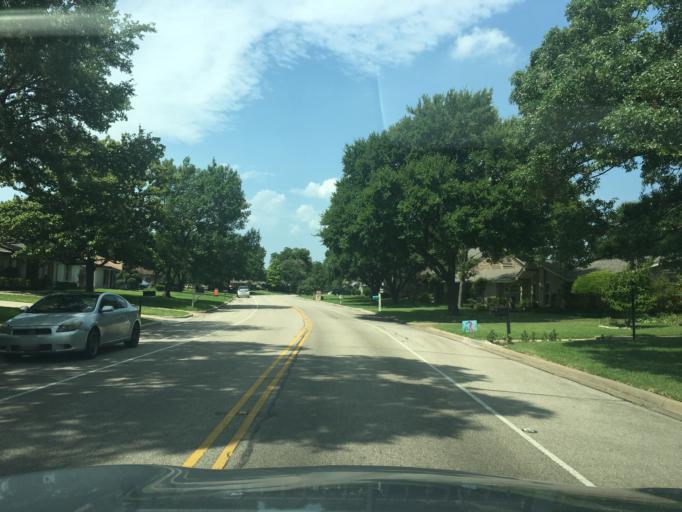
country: US
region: Texas
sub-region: Dallas County
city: Farmers Branch
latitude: 32.9335
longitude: -96.8677
